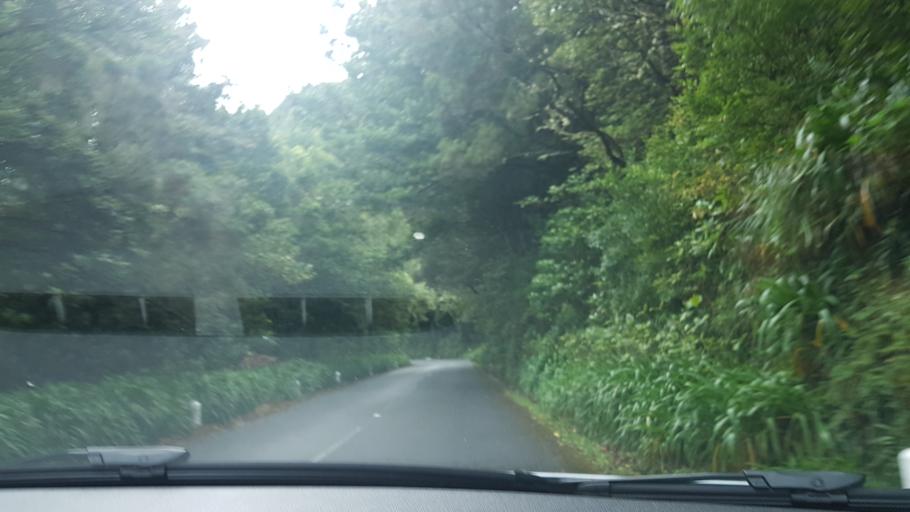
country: PT
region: Madeira
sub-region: Sao Vicente
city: Sao Vicente
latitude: 32.7553
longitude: -17.0170
